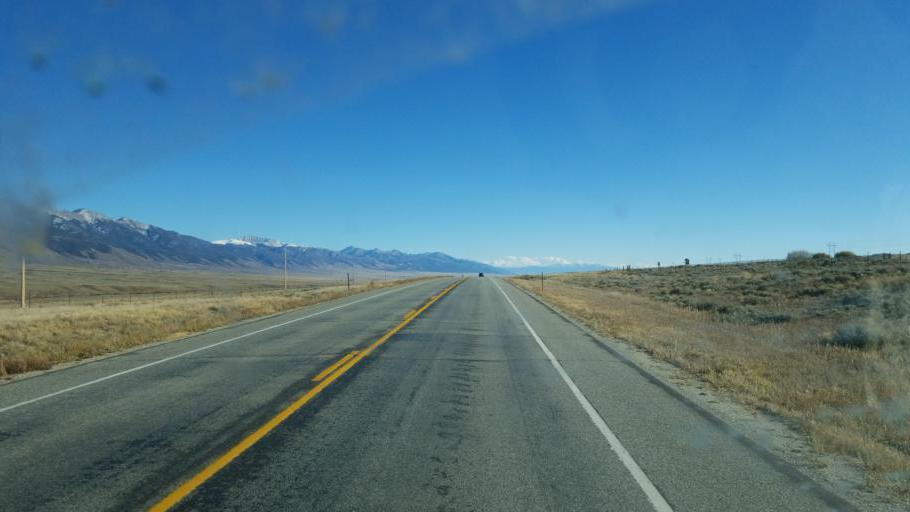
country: US
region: Colorado
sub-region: Chaffee County
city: Salida
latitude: 38.3766
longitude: -106.0455
